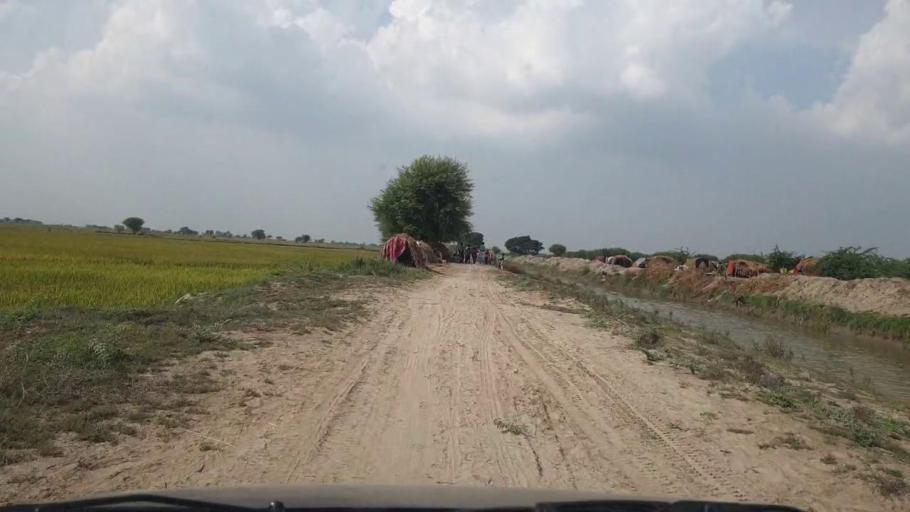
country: PK
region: Sindh
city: Badin
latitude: 24.5737
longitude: 68.6300
